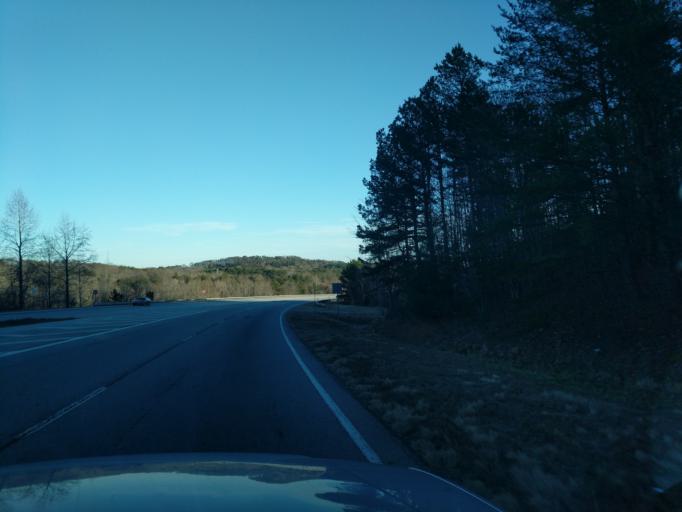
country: US
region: Georgia
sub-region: Stephens County
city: Toccoa
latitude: 34.5529
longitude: -83.3749
